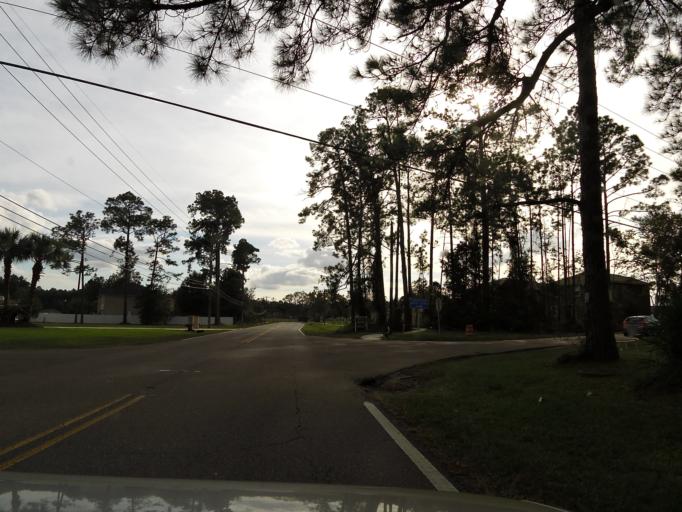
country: US
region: Florida
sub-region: Duval County
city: Jacksonville
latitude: 30.4536
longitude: -81.6842
